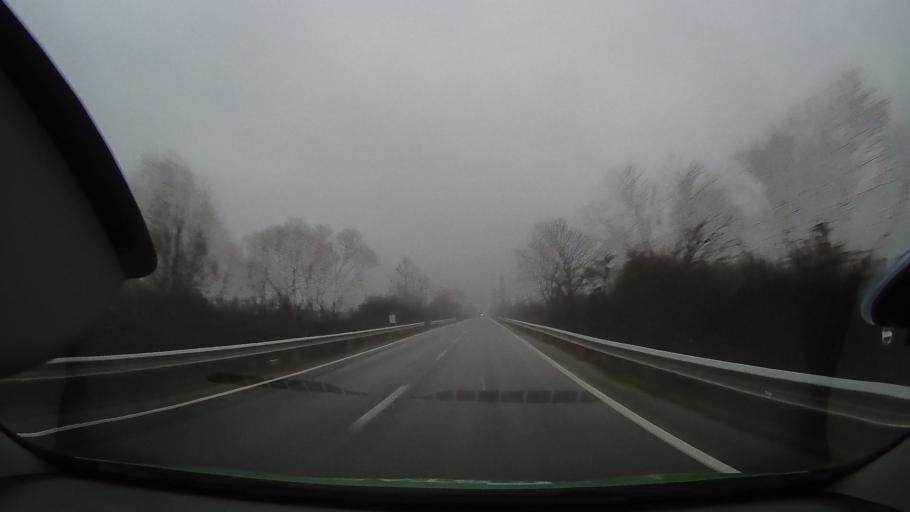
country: RO
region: Bihor
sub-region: Comuna Tinca
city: Tinca
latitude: 46.7586
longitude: 21.9354
